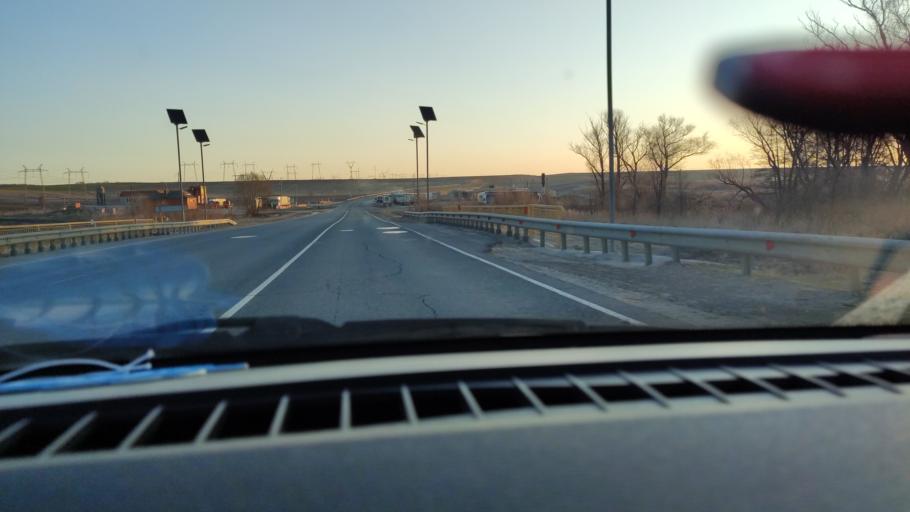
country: RU
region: Saratov
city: Sinodskoye
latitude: 51.9214
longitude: 46.5613
